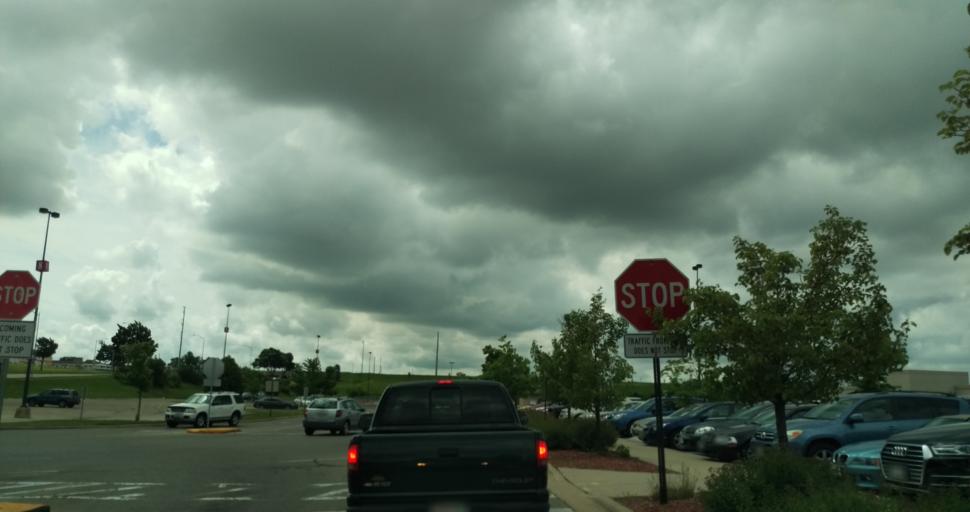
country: US
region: Wisconsin
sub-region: Dane County
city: Middleton
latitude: 43.0569
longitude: -89.5041
